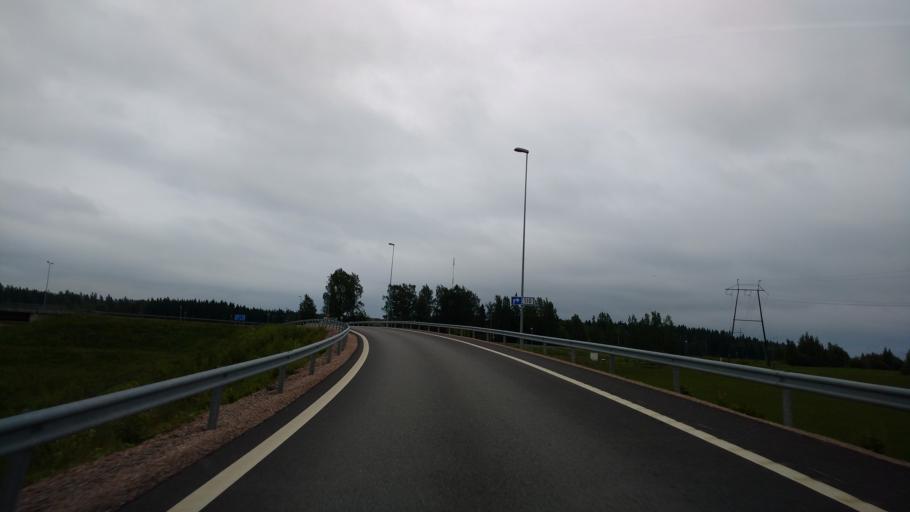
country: FI
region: Varsinais-Suomi
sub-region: Salo
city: Suomusjaervi
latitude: 60.3890
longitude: 23.5822
